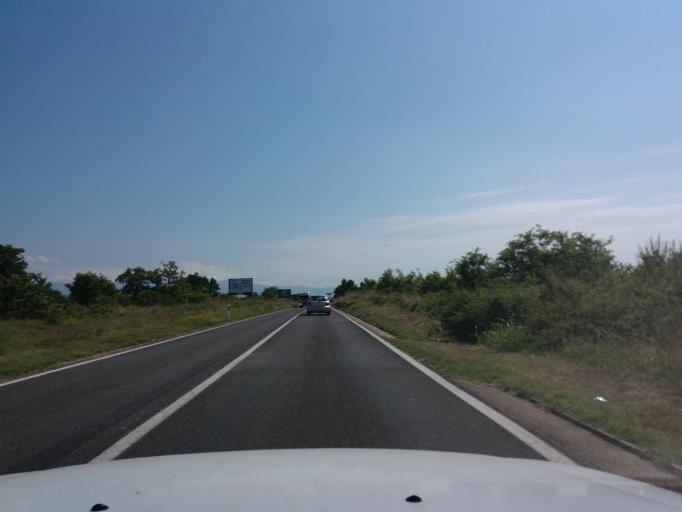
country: HR
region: Zadarska
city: Zadar
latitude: 44.1339
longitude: 15.3003
